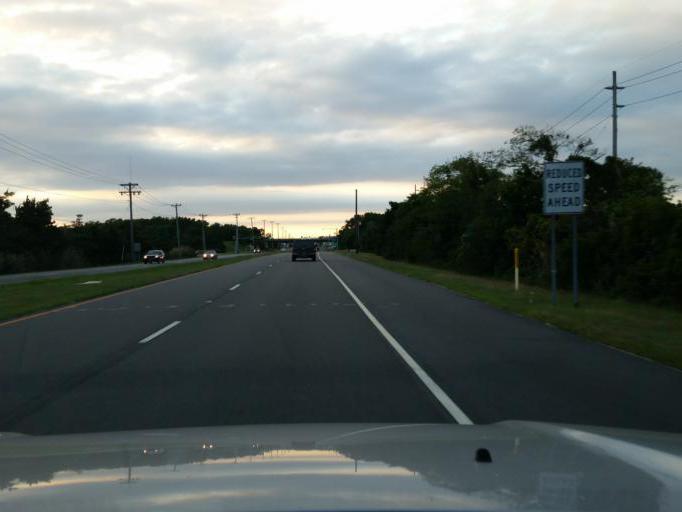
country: US
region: New Jersey
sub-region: Cape May County
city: Rio Grande
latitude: 39.0065
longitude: -74.8622
